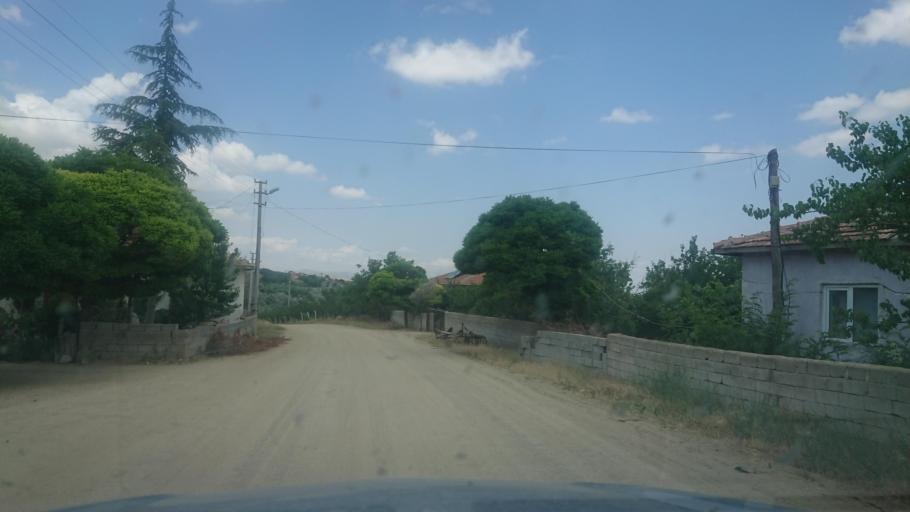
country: TR
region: Aksaray
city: Agacoren
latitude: 38.9322
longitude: 33.9567
